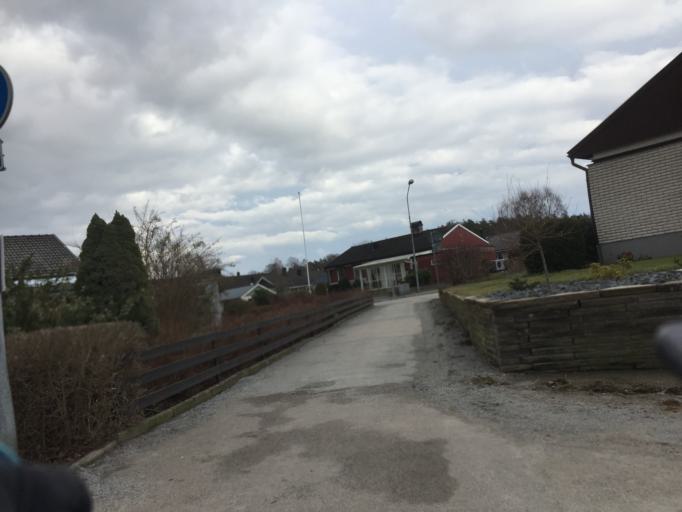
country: SE
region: Blekinge
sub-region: Karlshamns Kommun
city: Morrum
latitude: 56.1882
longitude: 14.7565
